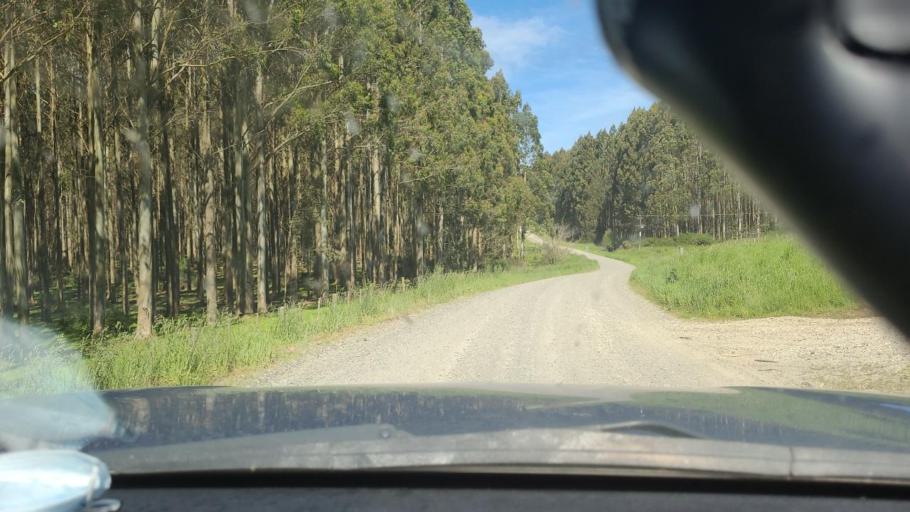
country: NZ
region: Southland
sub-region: Gore District
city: Gore
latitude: -46.5052
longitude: 168.9179
